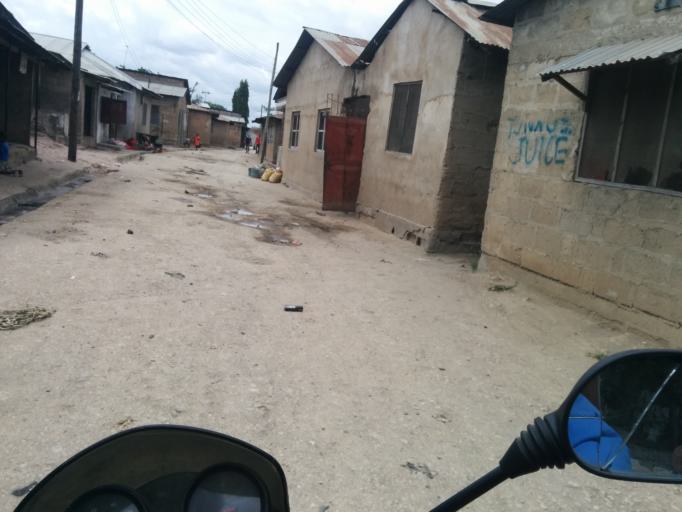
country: TZ
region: Dar es Salaam
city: Dar es Salaam
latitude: -6.8637
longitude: 39.2489
